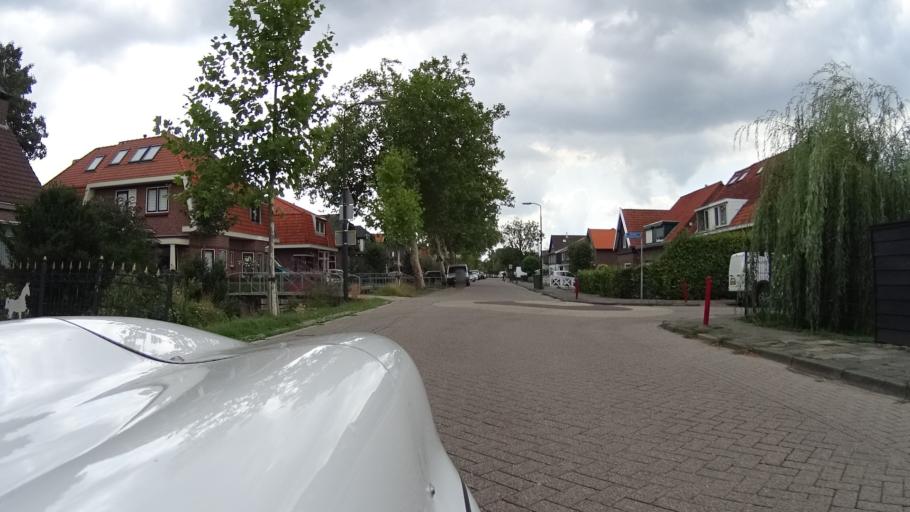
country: NL
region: South Holland
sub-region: Gemeente Hardinxveld-Giessendam
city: Boven-Hardinxveld
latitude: 51.8278
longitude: 4.8830
